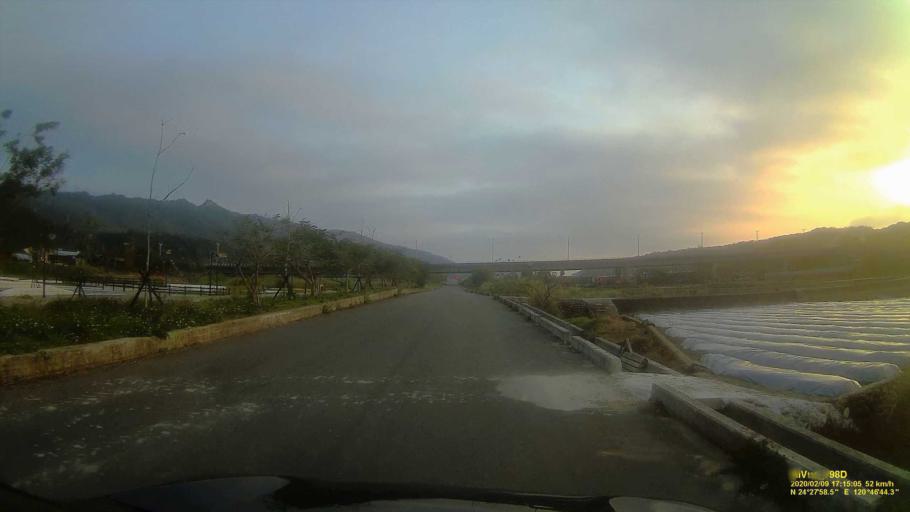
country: TW
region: Taiwan
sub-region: Miaoli
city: Miaoli
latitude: 24.4659
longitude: 120.7790
